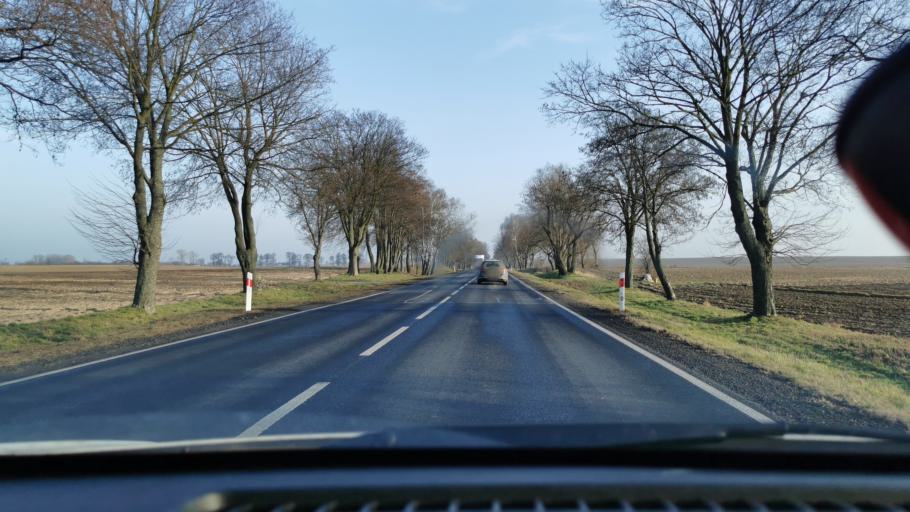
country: PL
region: Lodz Voivodeship
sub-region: Powiat sieradzki
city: Wroblew
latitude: 51.6230
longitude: 18.5766
